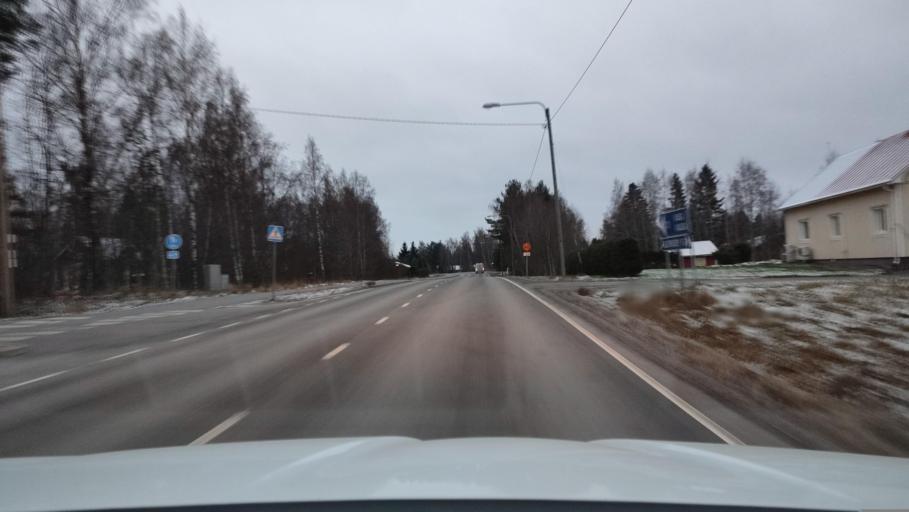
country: FI
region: Ostrobothnia
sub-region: Vaasa
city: Replot
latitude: 63.2256
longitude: 21.4112
